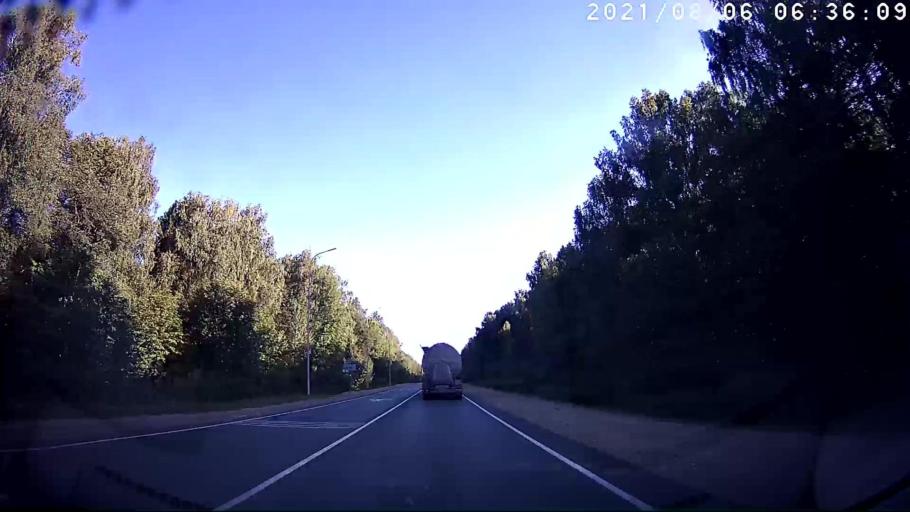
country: RU
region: Mariy-El
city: Suslonger
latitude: 56.2258
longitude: 48.2344
